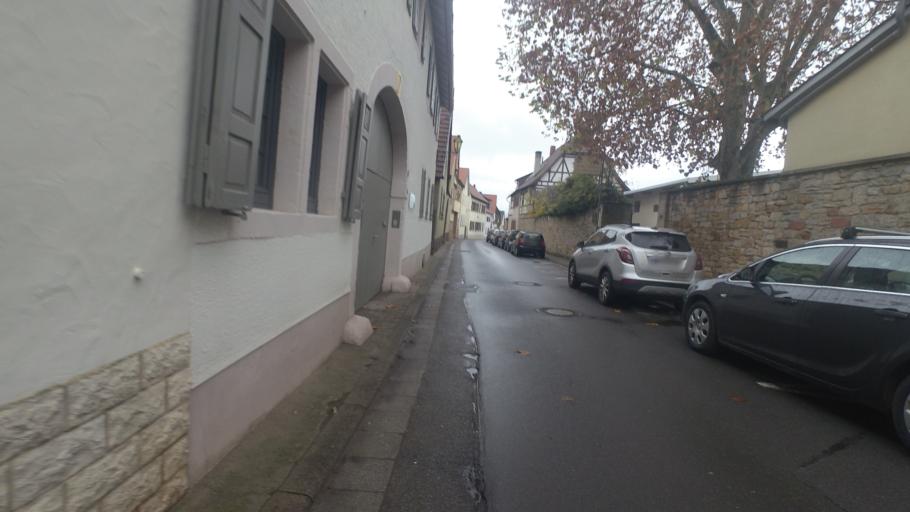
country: DE
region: Rheinland-Pfalz
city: Neustadt
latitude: 49.3730
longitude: 8.1632
